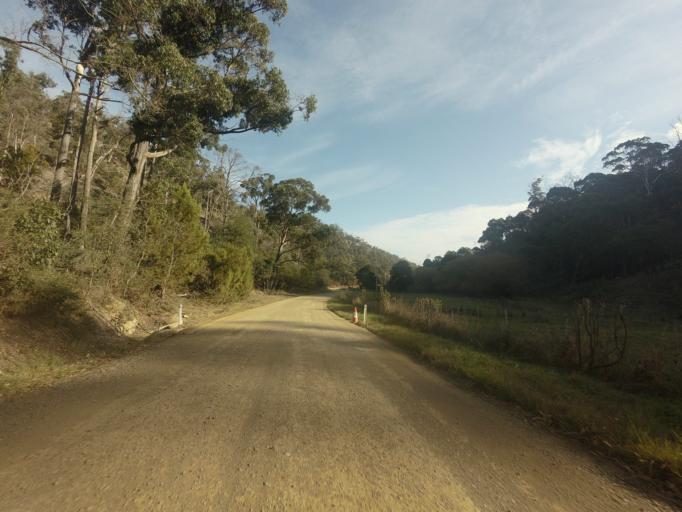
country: AU
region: Tasmania
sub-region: Brighton
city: Bridgewater
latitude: -42.5097
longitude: 147.4279
